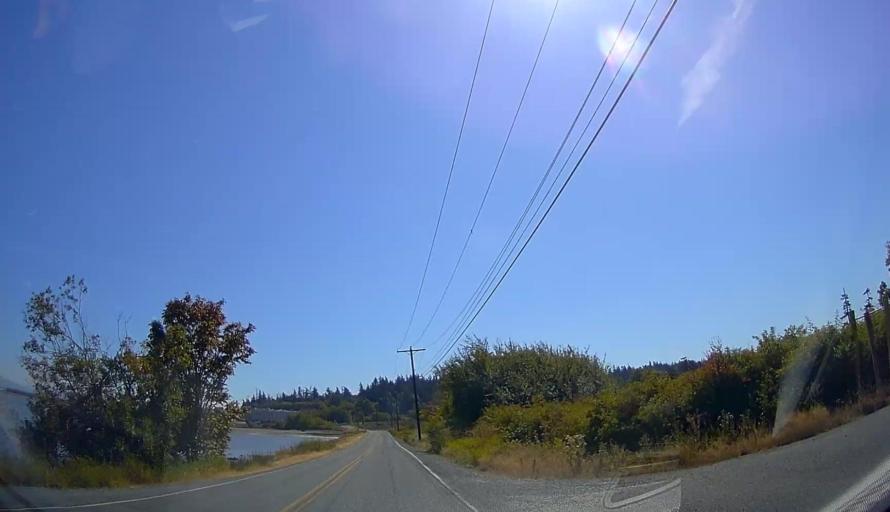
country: US
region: Washington
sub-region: Skagit County
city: Anacortes
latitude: 48.4689
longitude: -122.5398
